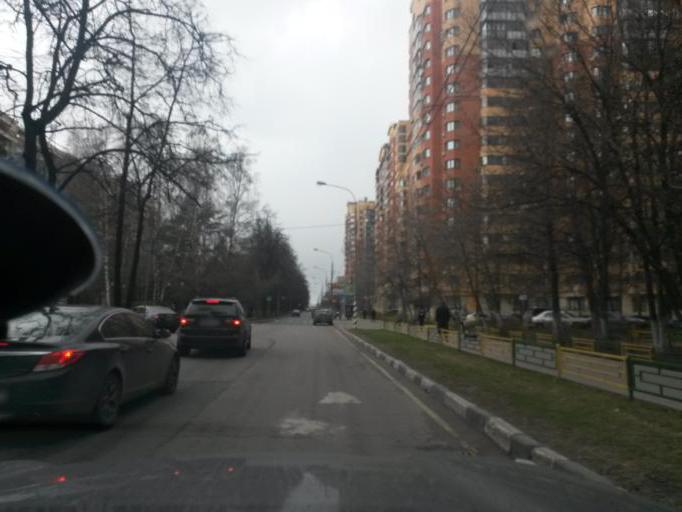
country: RU
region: Moskovskaya
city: Semenovskoye
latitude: 55.6759
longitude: 37.5394
